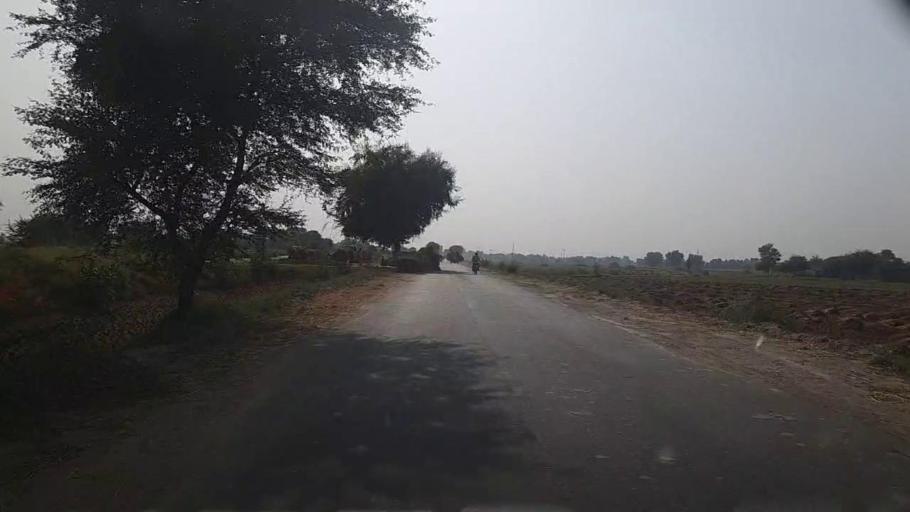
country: PK
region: Sindh
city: Kashmor
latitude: 28.4015
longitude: 69.5514
